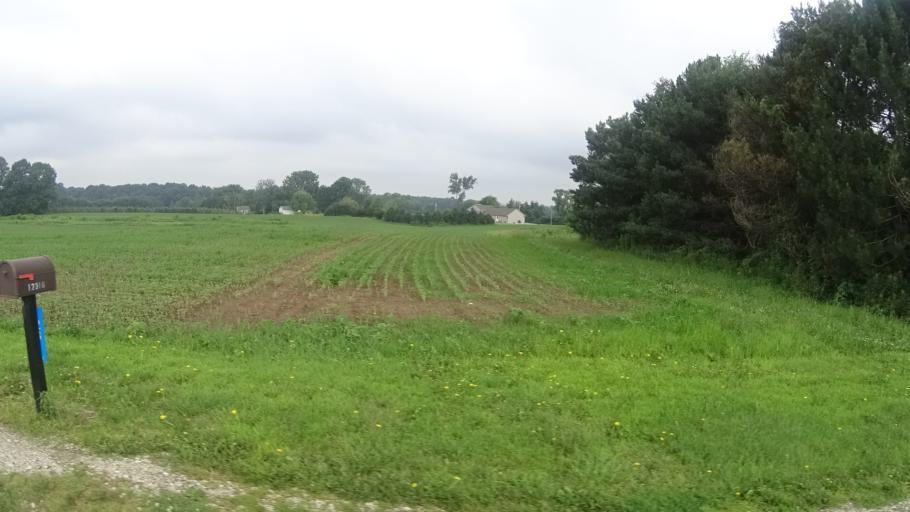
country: US
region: Ohio
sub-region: Erie County
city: Huron
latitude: 41.3140
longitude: -82.5018
